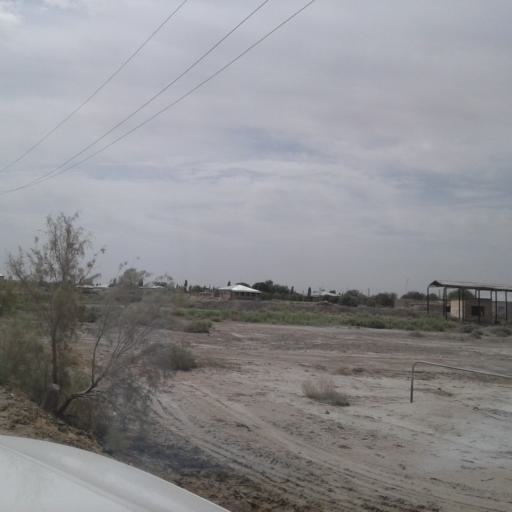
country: TM
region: Dasoguz
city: Tagta
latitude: 41.6044
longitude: 59.8426
